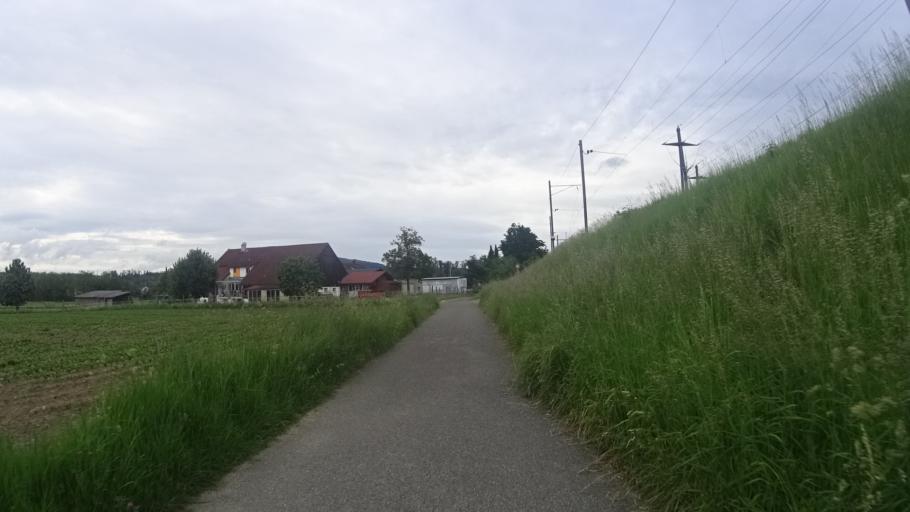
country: DE
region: Baden-Wuerttemberg
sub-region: Freiburg Region
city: Waldshut-Tiengen
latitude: 47.6087
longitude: 8.2196
